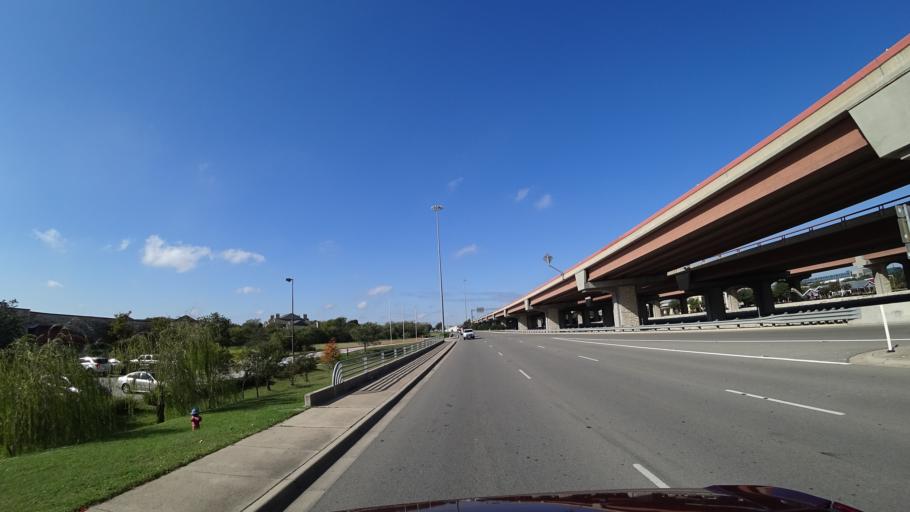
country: US
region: Texas
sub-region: Williamson County
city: Round Rock
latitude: 30.4794
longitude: -97.6810
